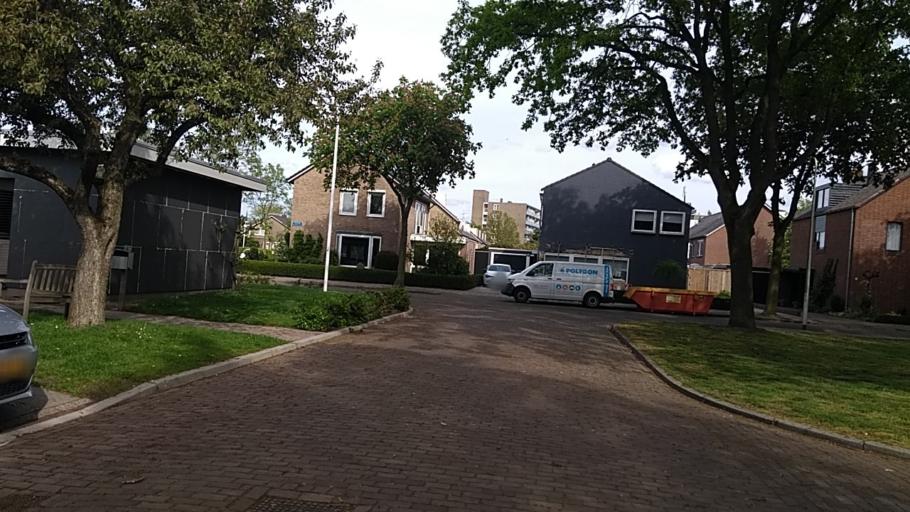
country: NL
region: Overijssel
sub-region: Gemeente Almelo
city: Almelo
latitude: 52.3716
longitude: 6.6587
